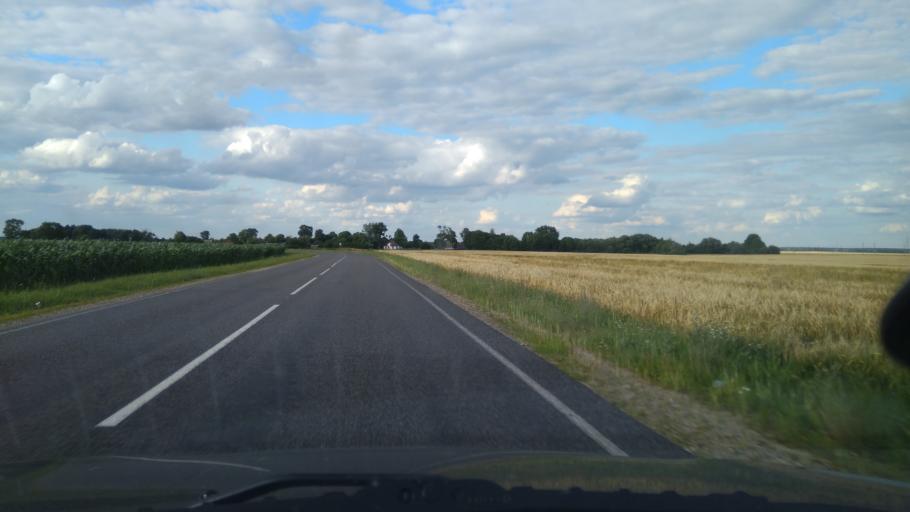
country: BY
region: Grodnenskaya
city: Masty
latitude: 53.3088
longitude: 24.6948
